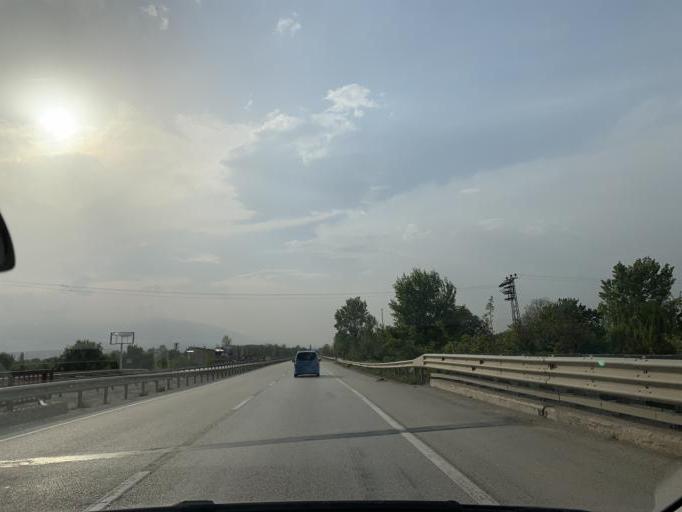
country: TR
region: Bursa
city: Kursunlu
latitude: 40.0358
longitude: 29.6057
